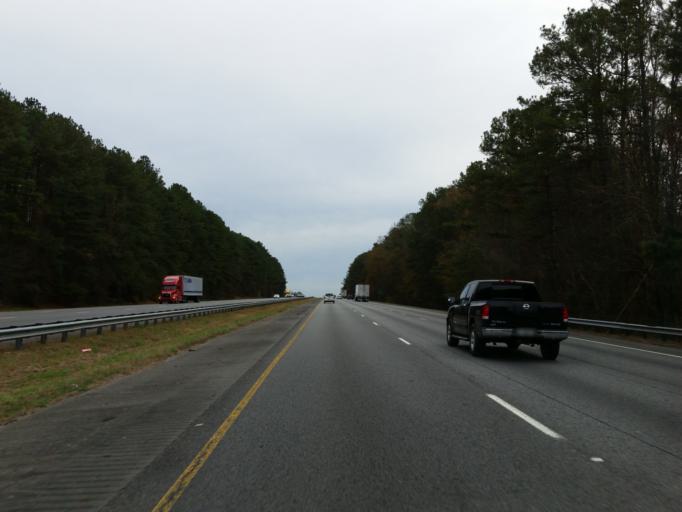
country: US
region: Georgia
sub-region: Monroe County
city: Forsyth
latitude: 33.1021
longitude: -84.0005
